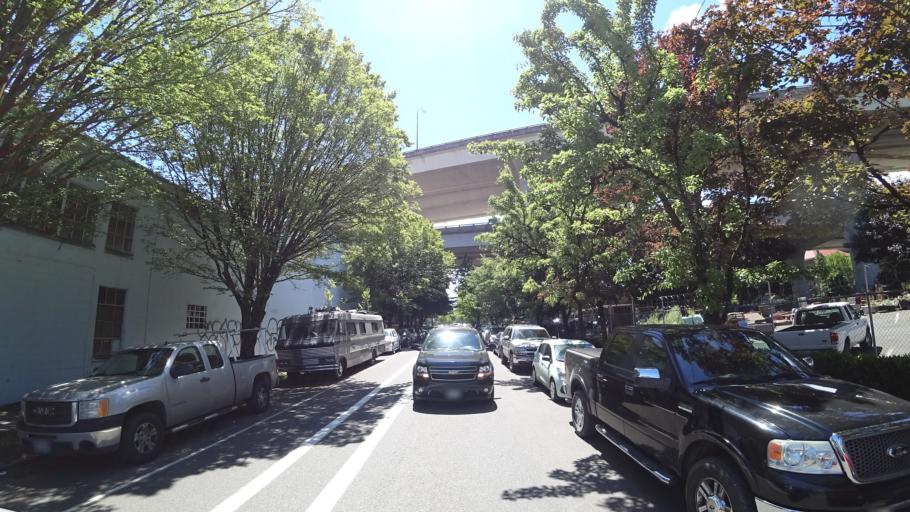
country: US
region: Oregon
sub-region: Multnomah County
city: Portland
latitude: 45.5355
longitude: -122.6897
